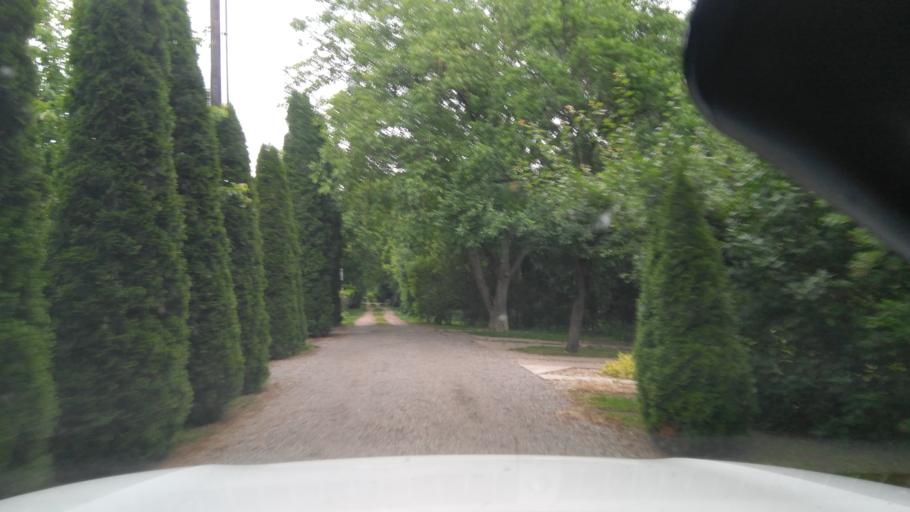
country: HU
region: Bekes
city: Doboz
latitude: 46.6717
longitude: 21.1876
